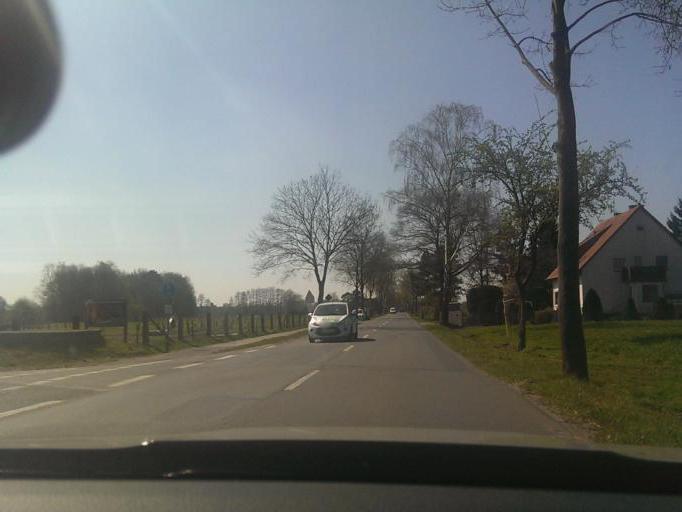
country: DE
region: Lower Saxony
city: Garbsen-Mitte
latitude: 52.5073
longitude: 9.6428
